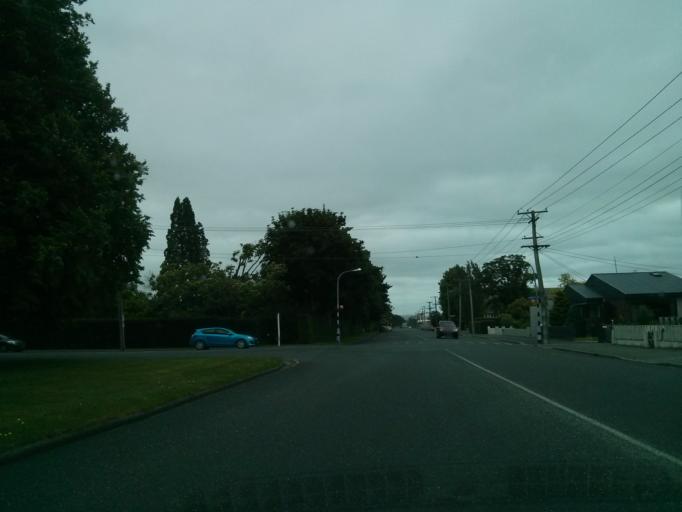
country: NZ
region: Southland
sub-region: Gore District
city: Gore
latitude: -46.0973
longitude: 168.9410
